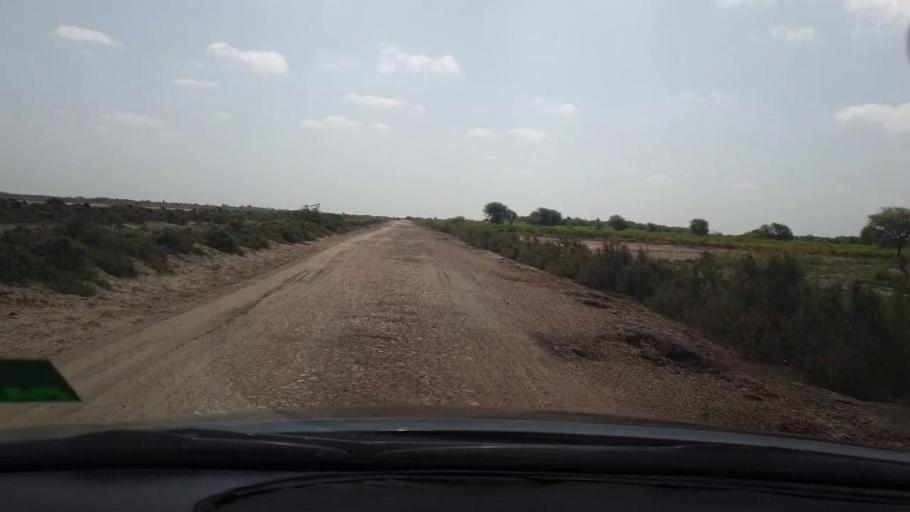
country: PK
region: Sindh
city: Tando Bago
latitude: 24.8355
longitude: 69.0518
